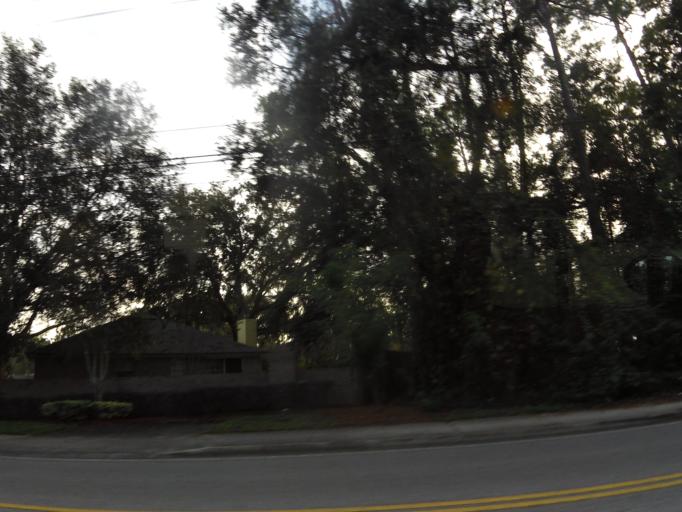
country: US
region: Florida
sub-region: Saint Johns County
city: Fruit Cove
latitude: 30.1609
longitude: -81.6292
